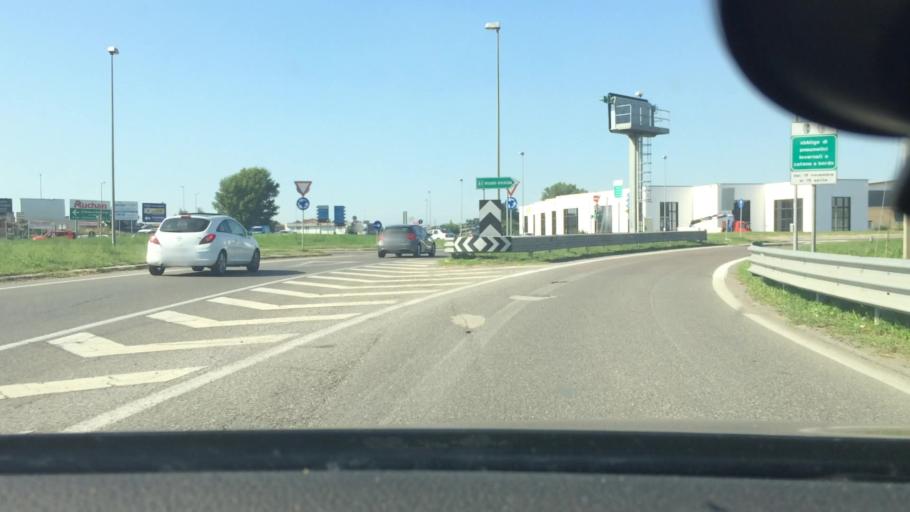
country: IT
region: Lombardy
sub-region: Provincia di Lodi
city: Guardamiglio
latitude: 45.1052
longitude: 9.6849
